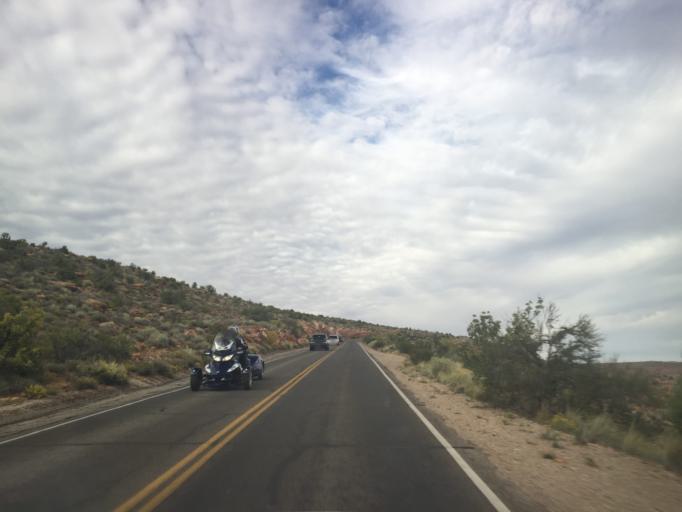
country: US
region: Utah
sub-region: Grand County
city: Moab
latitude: 38.7245
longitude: -109.5408
